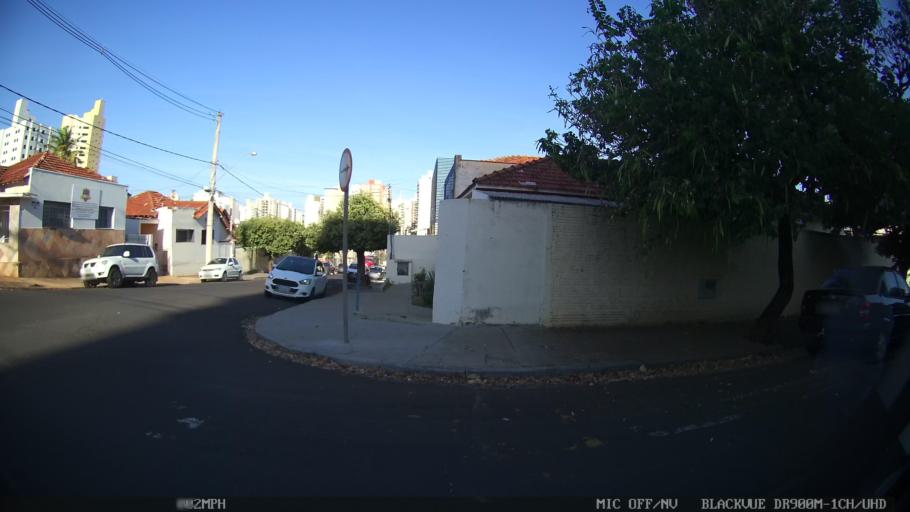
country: BR
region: Sao Paulo
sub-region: Sao Jose Do Rio Preto
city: Sao Jose do Rio Preto
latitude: -20.8117
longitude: -49.3905
